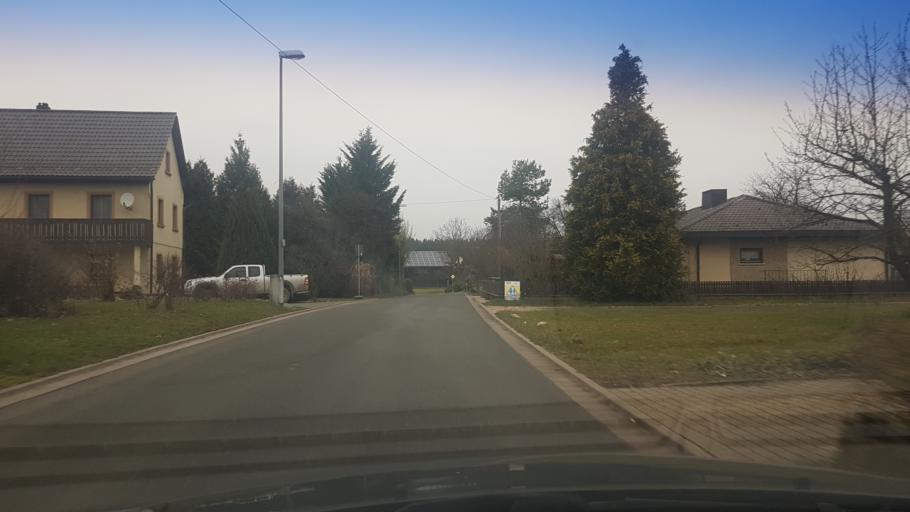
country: DE
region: Bavaria
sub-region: Upper Franconia
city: Stadelhofen
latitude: 50.0162
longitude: 11.2447
